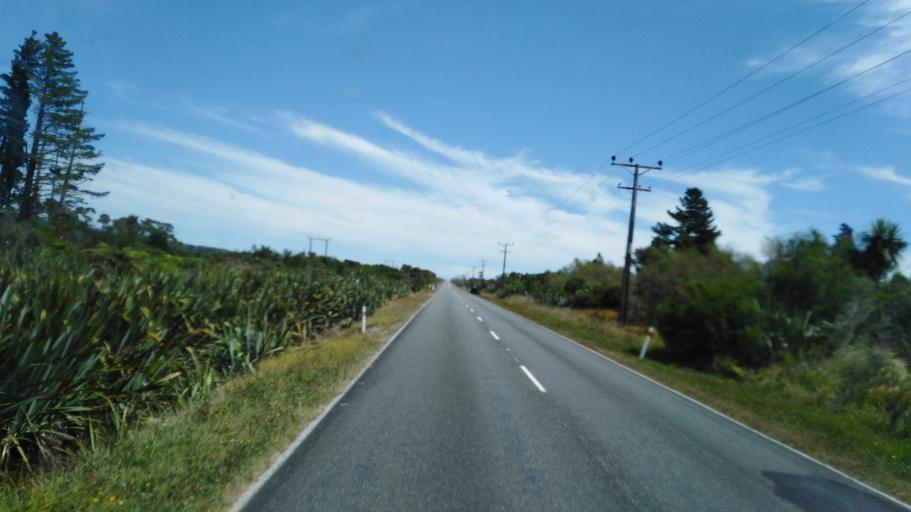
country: NZ
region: West Coast
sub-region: Buller District
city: Westport
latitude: -41.7444
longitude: 171.6879
